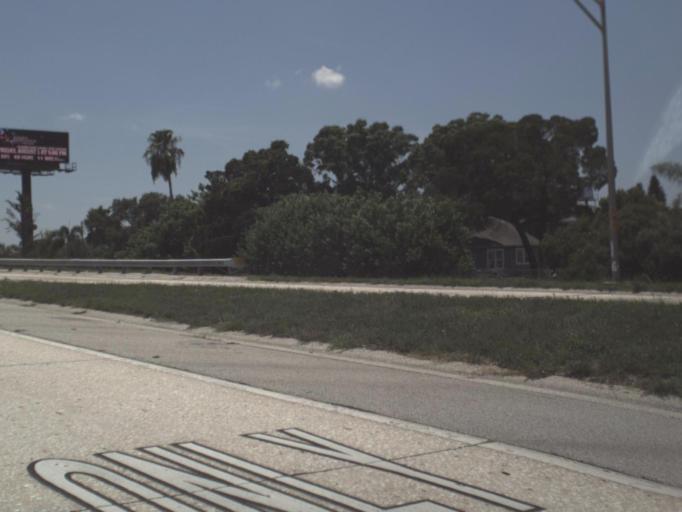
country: US
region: Florida
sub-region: Pinellas County
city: Lealman
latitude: 27.8192
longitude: -82.6649
